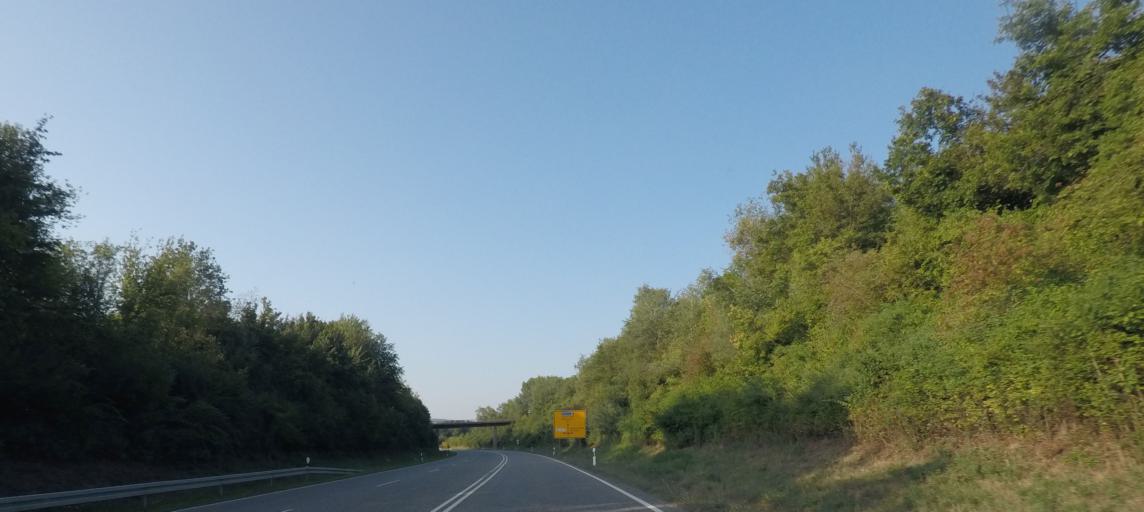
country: DE
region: Saarland
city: Heusweiler
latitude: 49.3694
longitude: 6.9246
